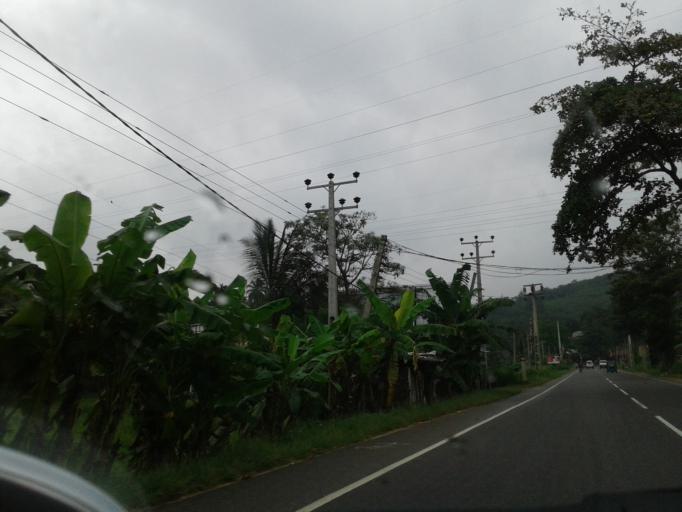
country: LK
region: Western
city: Gampaha
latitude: 7.2372
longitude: 80.2267
